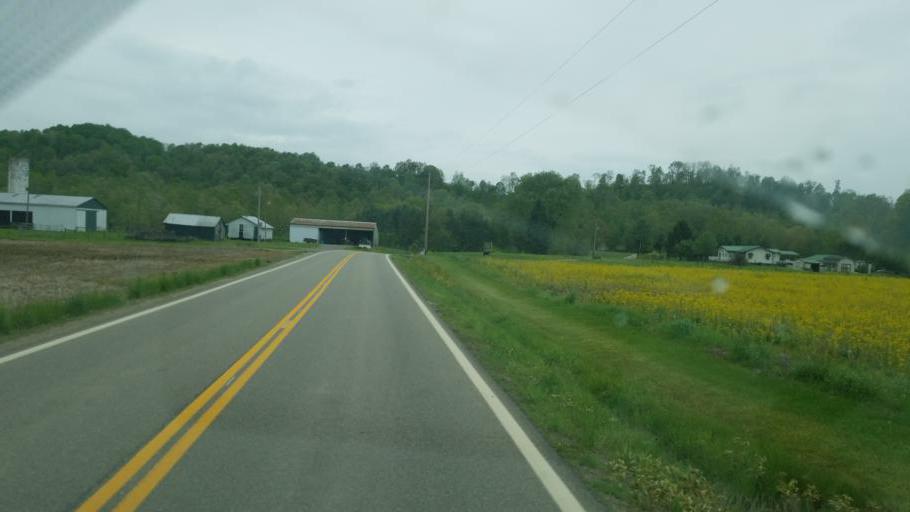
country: US
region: Ohio
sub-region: Guernsey County
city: Mantua
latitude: 40.1523
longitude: -81.5988
